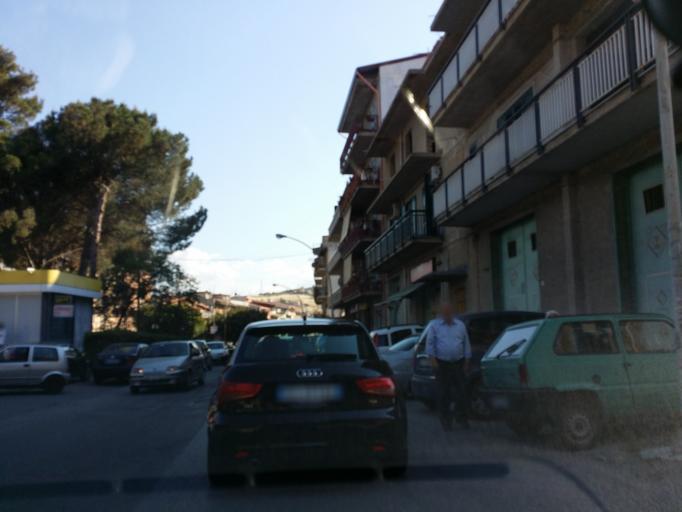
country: IT
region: Sicily
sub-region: Palermo
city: Misilmeri
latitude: 38.0259
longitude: 13.4474
